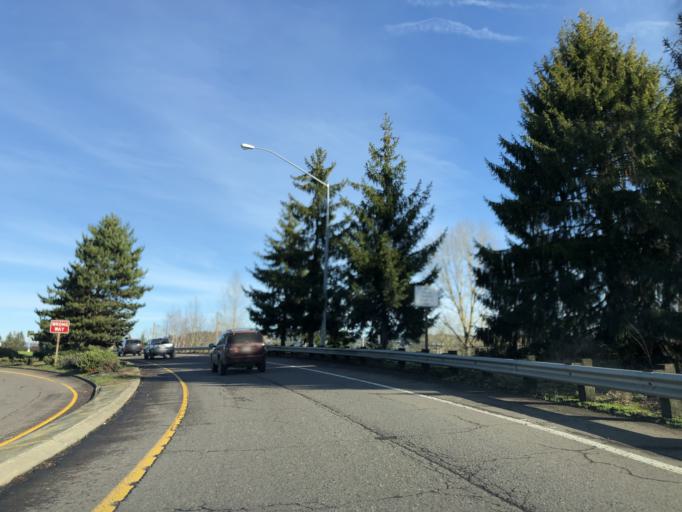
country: US
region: Oregon
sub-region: Clackamas County
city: Oregon City
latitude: 45.3642
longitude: -122.6001
